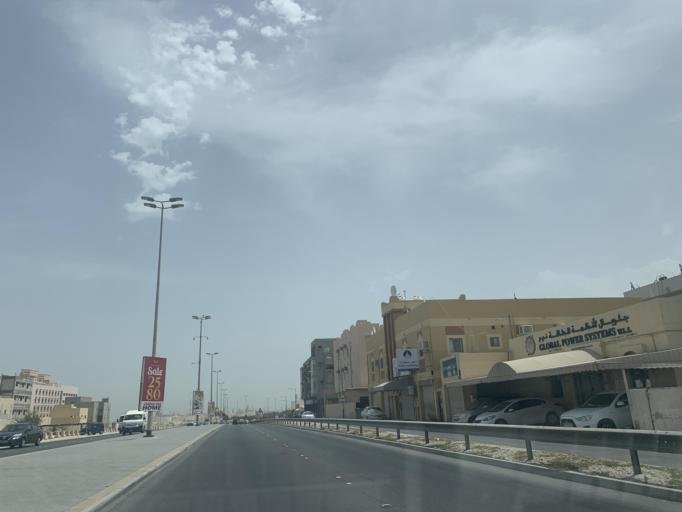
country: BH
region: Northern
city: Ar Rifa'
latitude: 26.1197
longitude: 50.5797
